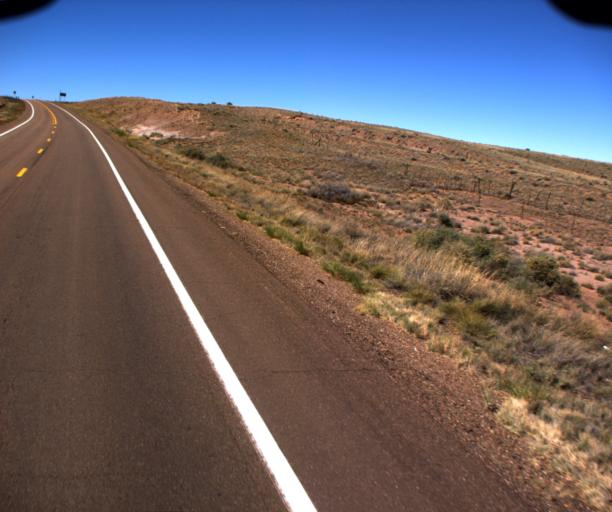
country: US
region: Arizona
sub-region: Apache County
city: Saint Johns
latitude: 34.5101
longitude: -109.4420
